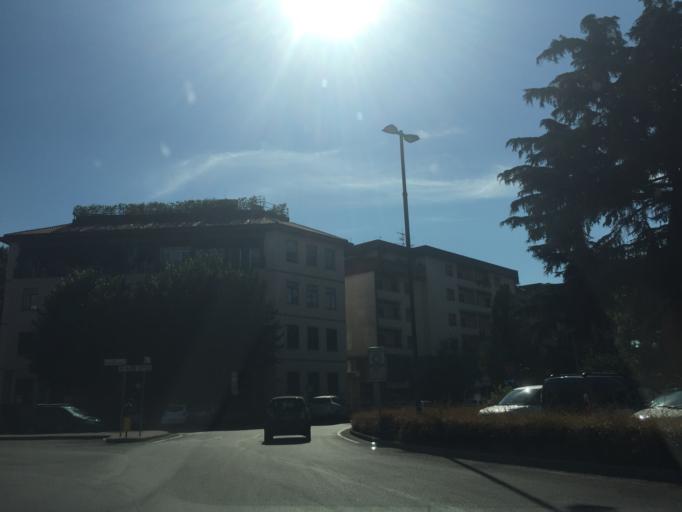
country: IT
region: Tuscany
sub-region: Provincia di Lucca
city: Lucca
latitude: 43.8489
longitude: 10.5065
